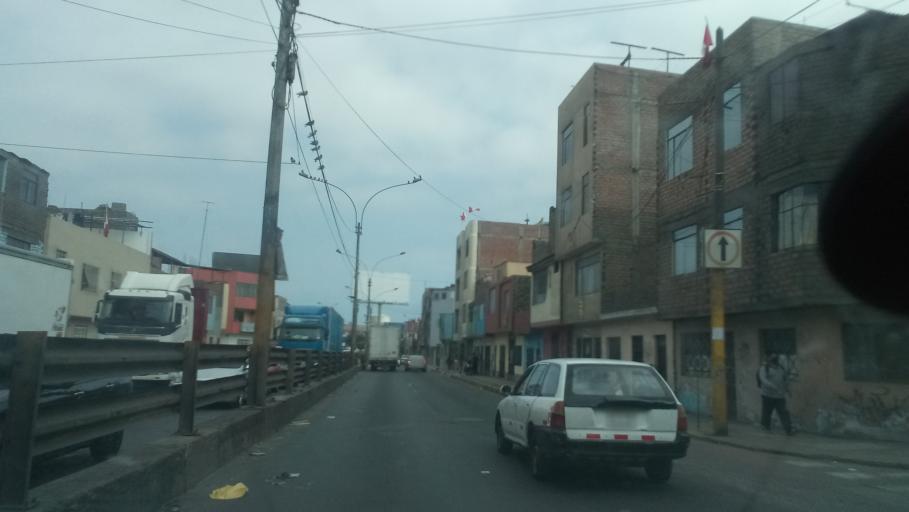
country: PE
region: Callao
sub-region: Callao
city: Callao
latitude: -12.0329
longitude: -77.0780
